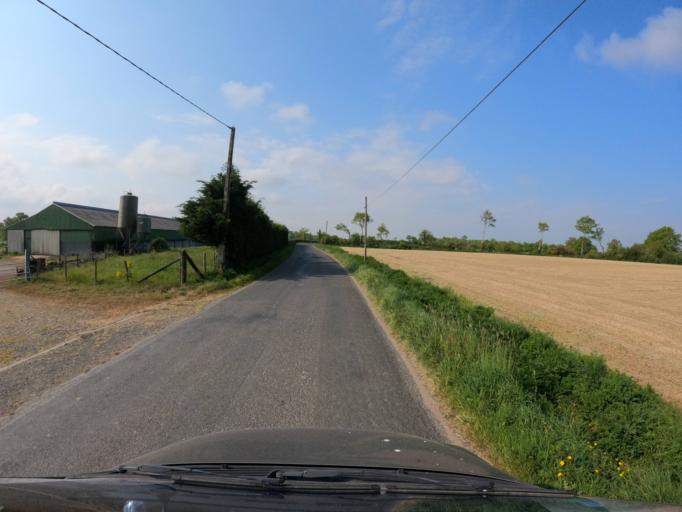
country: FR
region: Pays de la Loire
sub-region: Departement de Maine-et-Loire
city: Roussay
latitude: 47.0620
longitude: -1.0873
